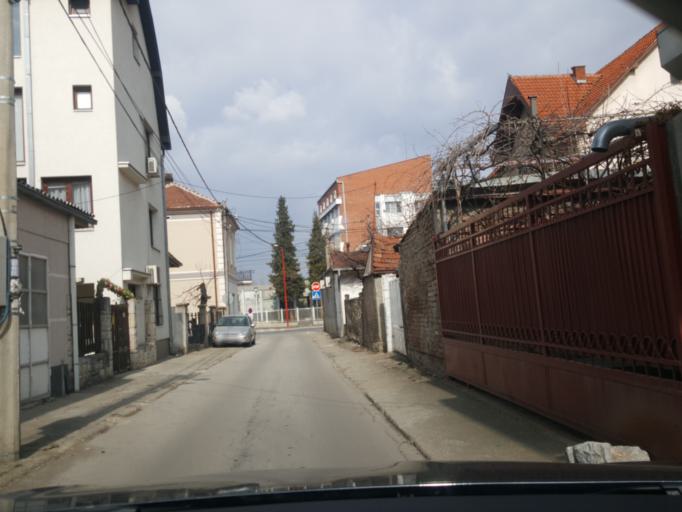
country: RS
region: Central Serbia
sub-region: Nisavski Okrug
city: Nis
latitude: 43.3149
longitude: 21.8717
